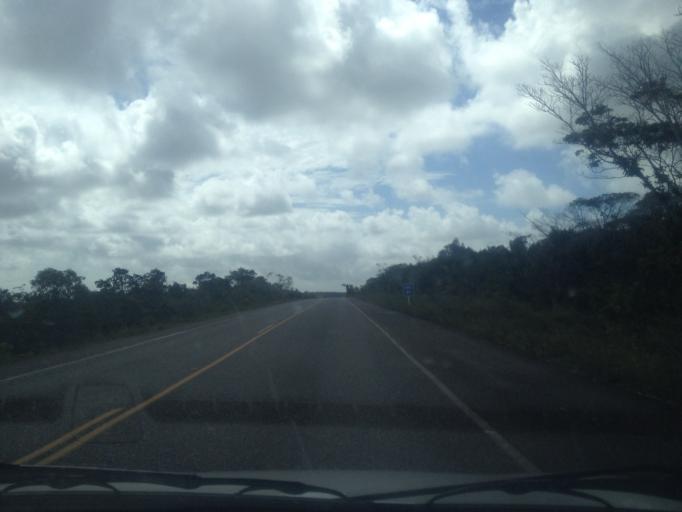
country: BR
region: Bahia
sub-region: Entre Rios
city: Entre Rios
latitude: -12.2537
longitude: -37.8640
